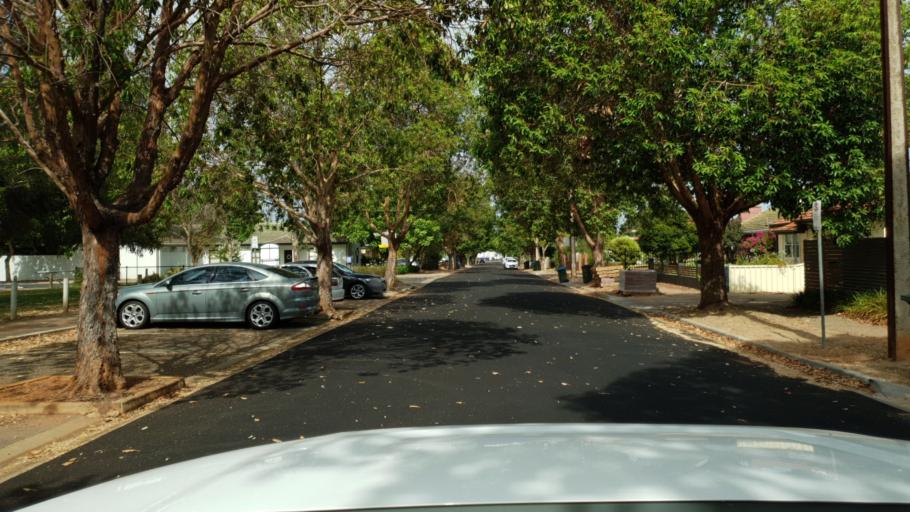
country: AU
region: South Australia
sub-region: Mitcham
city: Clarence Gardens
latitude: -34.9725
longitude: 138.5770
